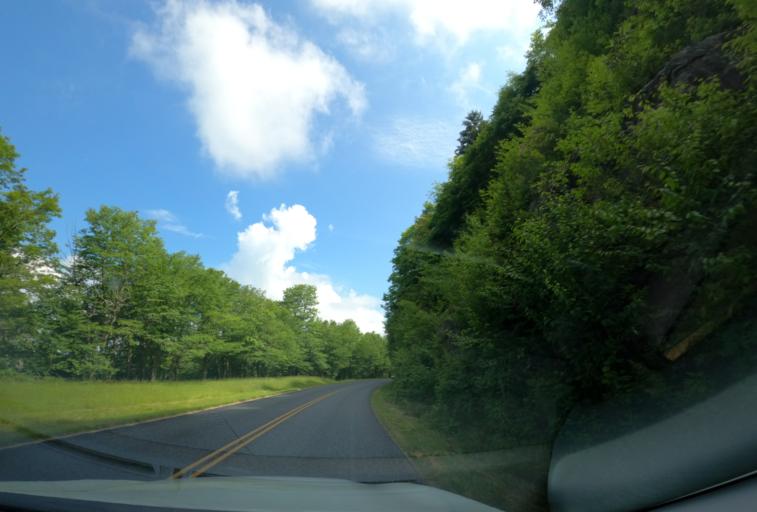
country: US
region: North Carolina
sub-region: Haywood County
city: Hazelwood
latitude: 35.3834
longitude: -83.0304
